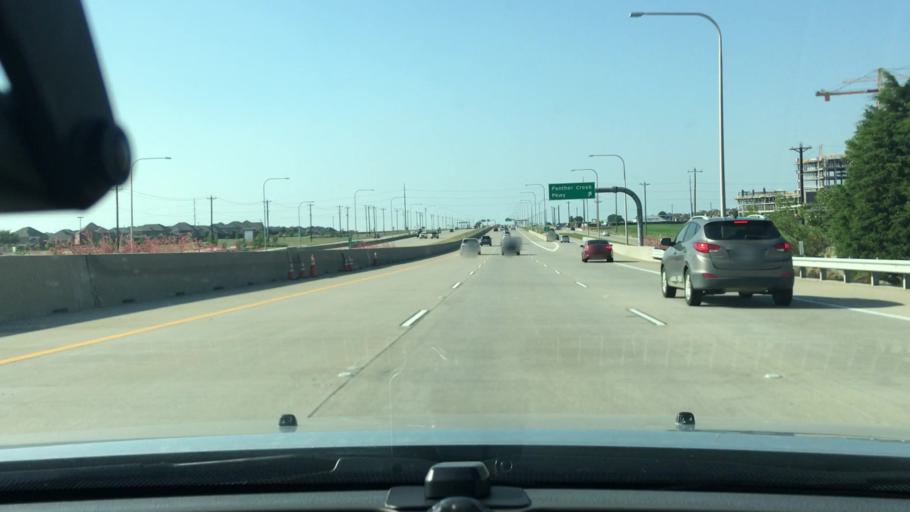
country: US
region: Texas
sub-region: Collin County
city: Frisco
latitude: 33.1768
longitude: -96.8394
